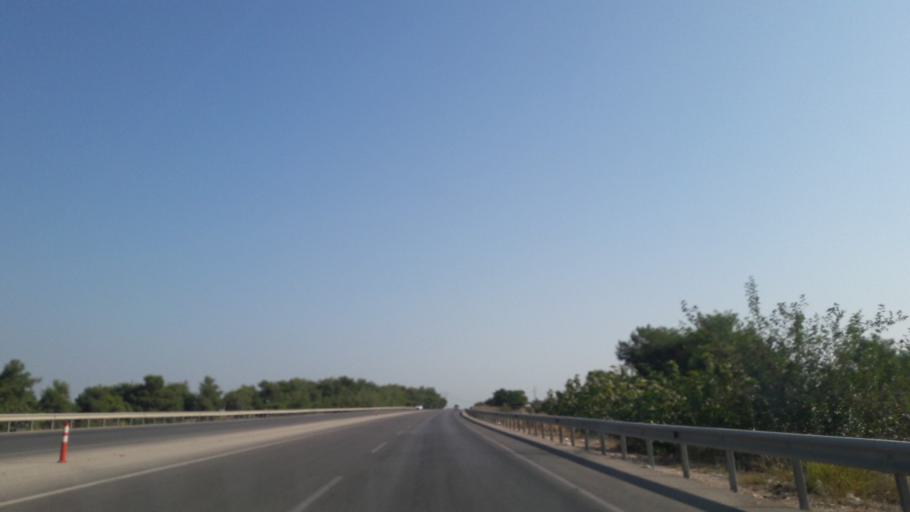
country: TR
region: Adana
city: Sagkaya
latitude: 37.1256
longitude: 35.5184
